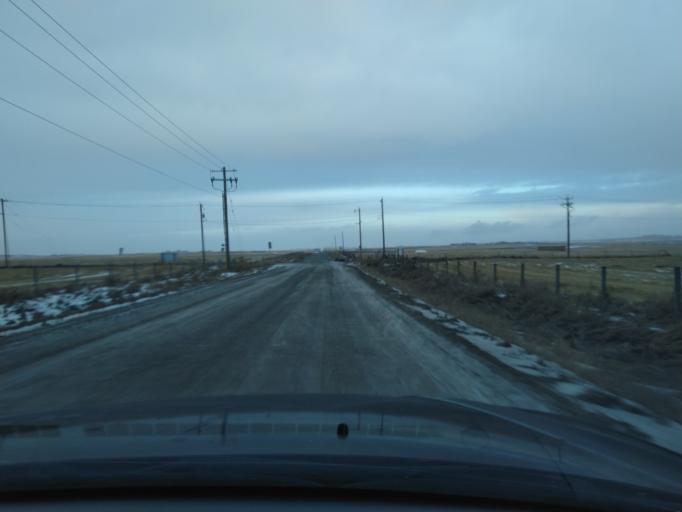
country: CA
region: Alberta
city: Airdrie
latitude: 51.1827
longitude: -114.0248
